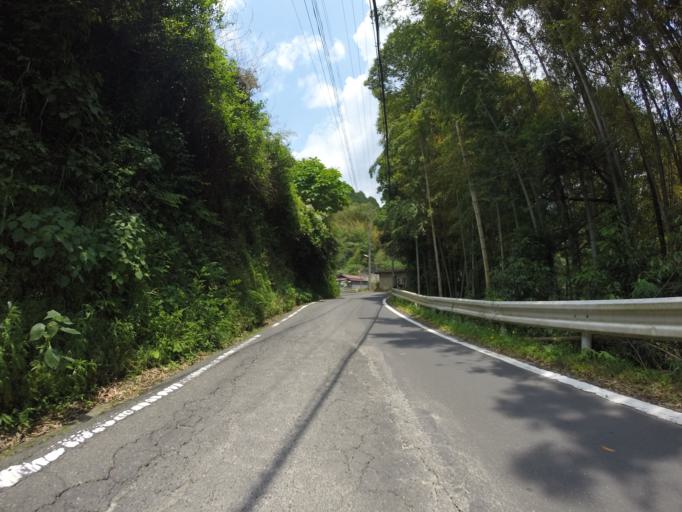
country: JP
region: Shizuoka
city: Shizuoka-shi
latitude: 35.1146
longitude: 138.3074
